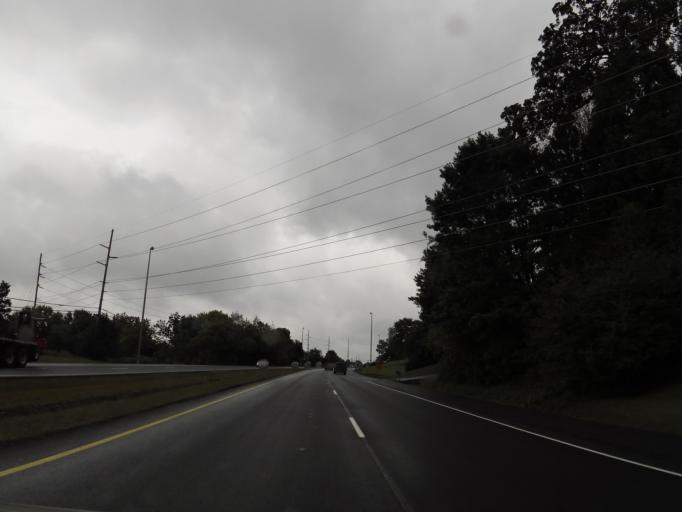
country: US
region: Tennessee
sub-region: Bradley County
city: Hopewell
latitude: 35.2006
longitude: -84.8894
